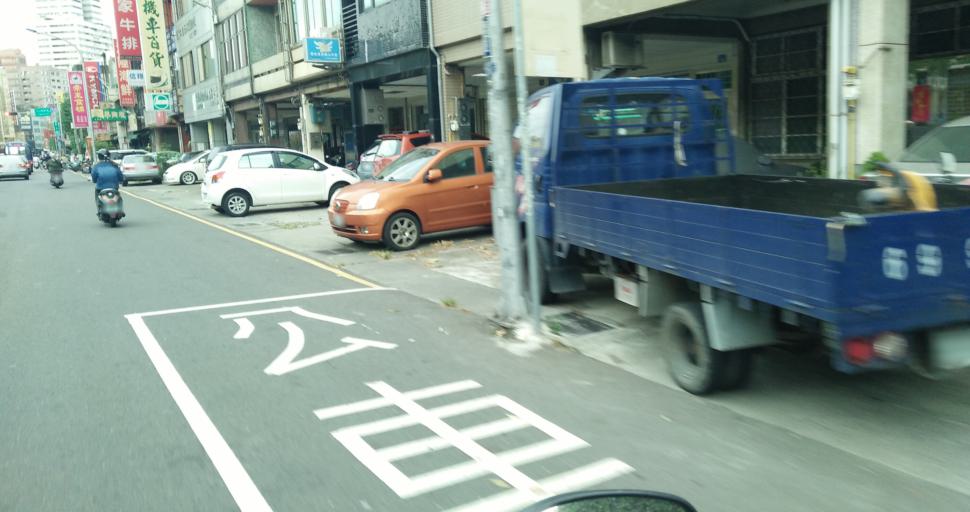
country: TW
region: Taiwan
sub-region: Hsinchu
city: Hsinchu
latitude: 24.8023
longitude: 120.9601
